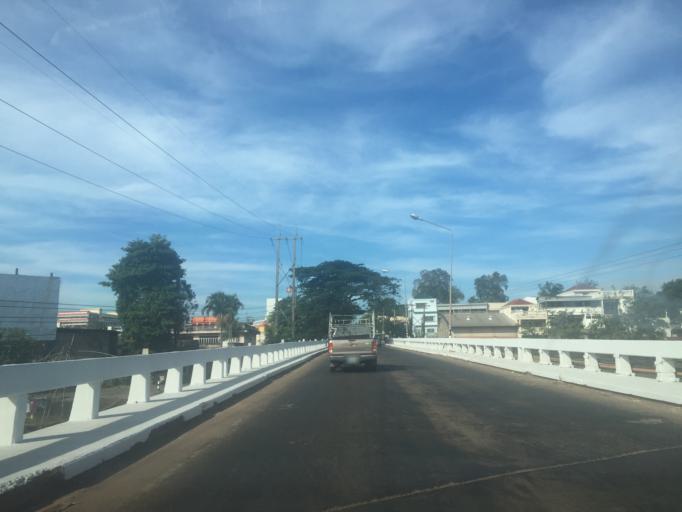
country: TH
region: Changwat Udon Thani
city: Kumphawapi
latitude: 17.1108
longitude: 103.0210
